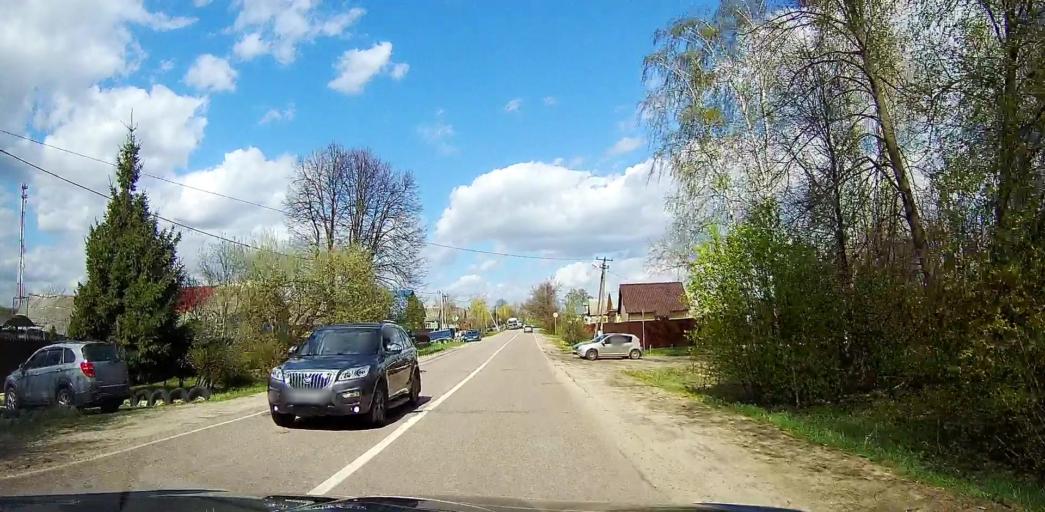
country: RU
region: Moskovskaya
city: Davydovo
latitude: 55.5737
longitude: 38.8196
